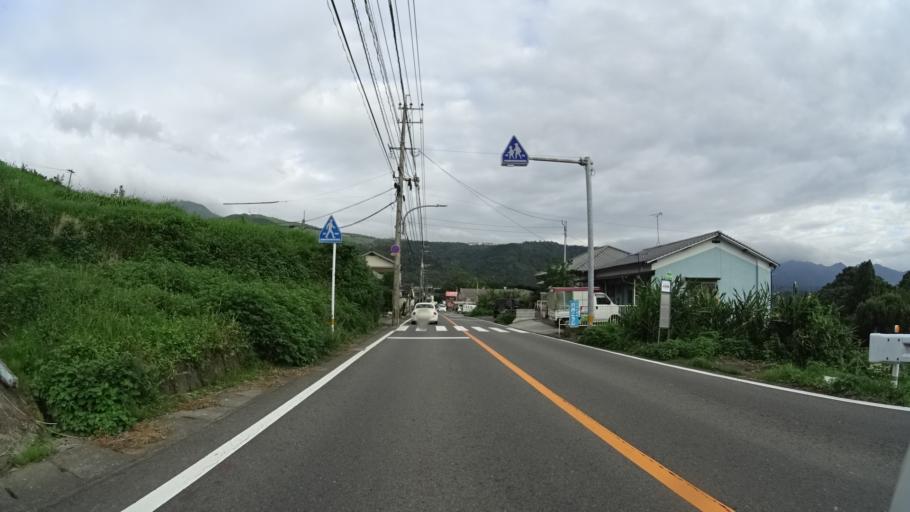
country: JP
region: Oita
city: Beppu
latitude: 33.3205
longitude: 131.4804
